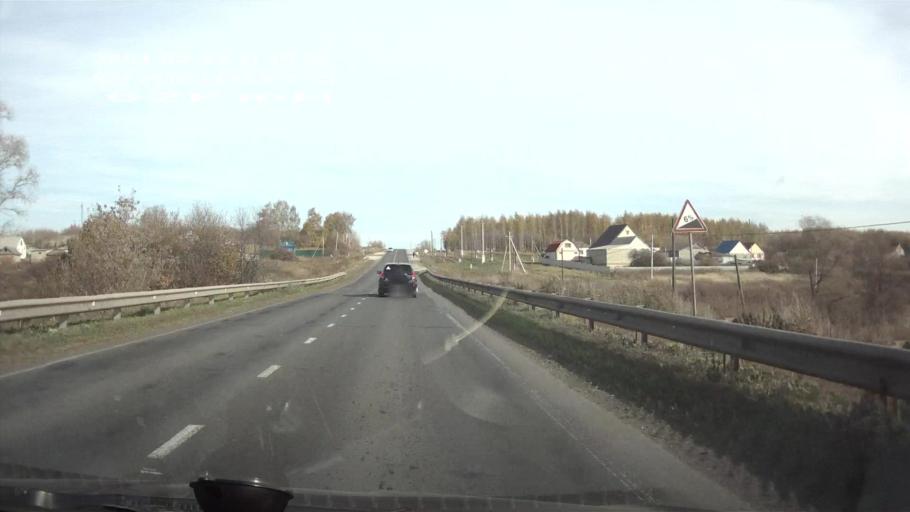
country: RU
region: Mordoviya
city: Atyashevo
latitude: 54.5620
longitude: 45.9796
